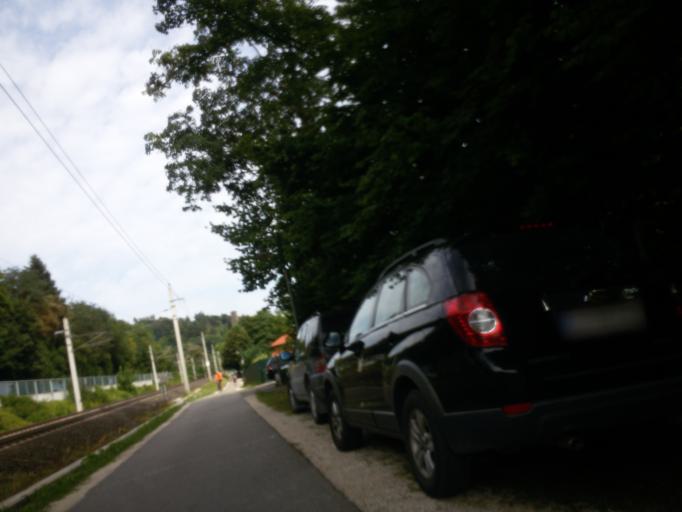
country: AT
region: Carinthia
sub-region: Politischer Bezirk Klagenfurt Land
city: Keutschach am See
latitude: 46.6275
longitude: 14.2356
